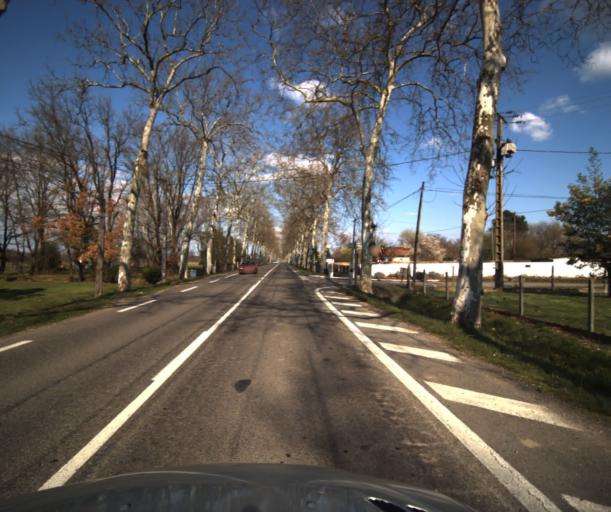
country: FR
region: Midi-Pyrenees
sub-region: Departement du Tarn-et-Garonne
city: Montbeton
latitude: 43.9789
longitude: 1.2888
